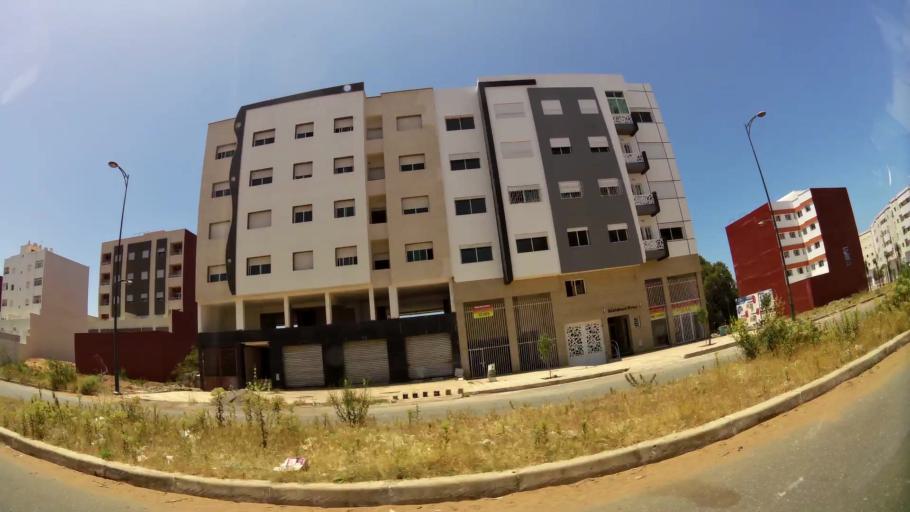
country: MA
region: Gharb-Chrarda-Beni Hssen
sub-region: Kenitra Province
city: Kenitra
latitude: 34.2701
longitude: -6.6277
